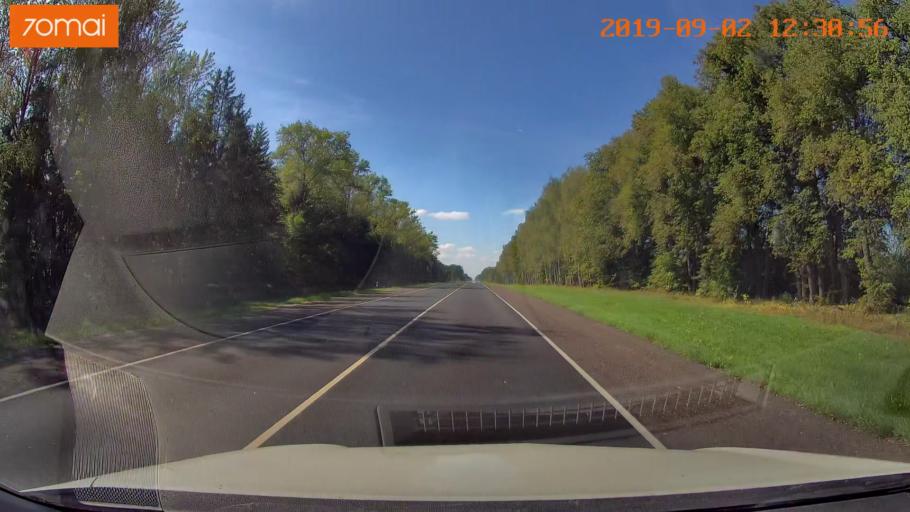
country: RU
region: Smolensk
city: Shumyachi
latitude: 53.8284
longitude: 32.4624
